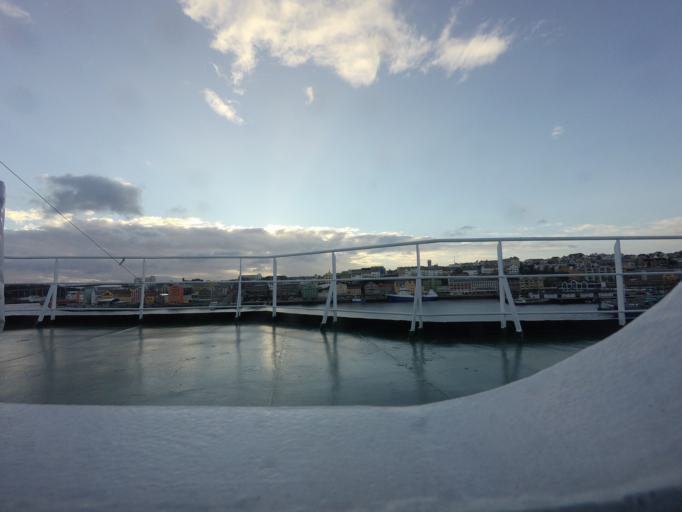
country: NO
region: More og Romsdal
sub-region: Kristiansund
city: Kristiansund
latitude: 63.1128
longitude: 7.7388
